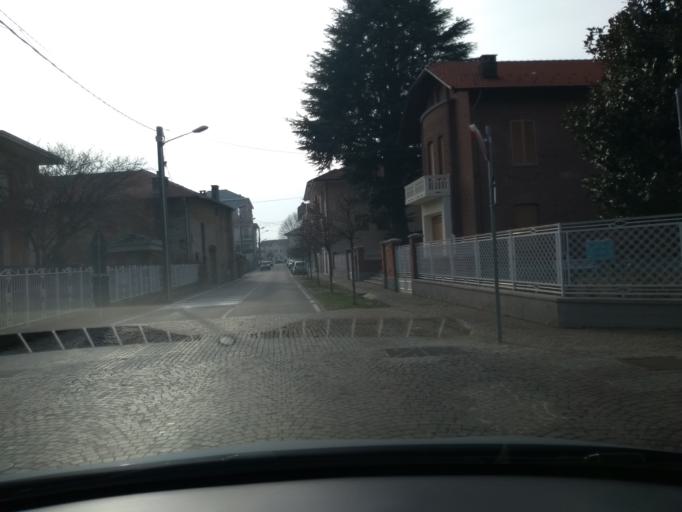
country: IT
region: Piedmont
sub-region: Provincia di Torino
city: Balangero
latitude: 45.2683
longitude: 7.5199
